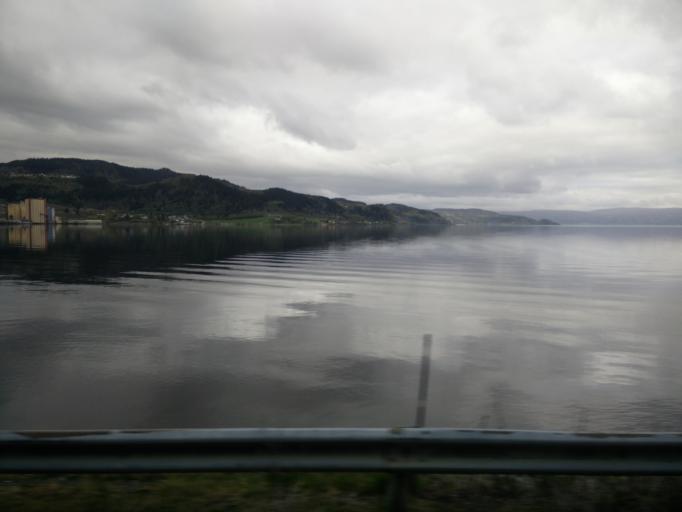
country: NO
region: Sor-Trondelag
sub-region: Melhus
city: Melhus
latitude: 63.3187
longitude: 10.1930
